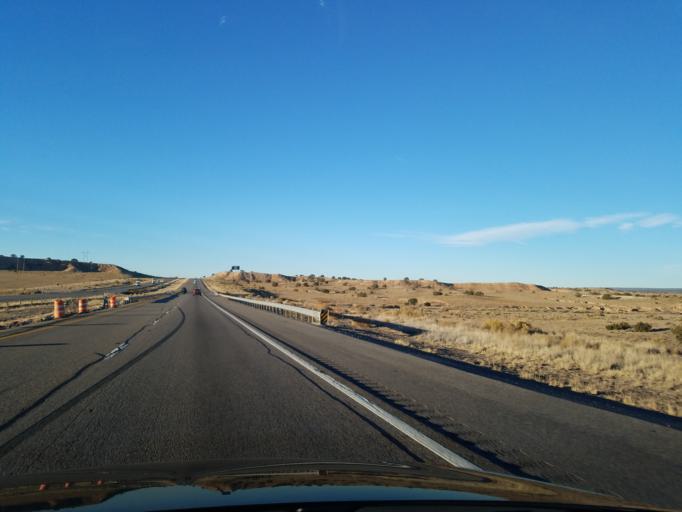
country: US
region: New Mexico
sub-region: Sandoval County
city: San Felipe Pueblo
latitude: 35.4359
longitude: -106.3771
